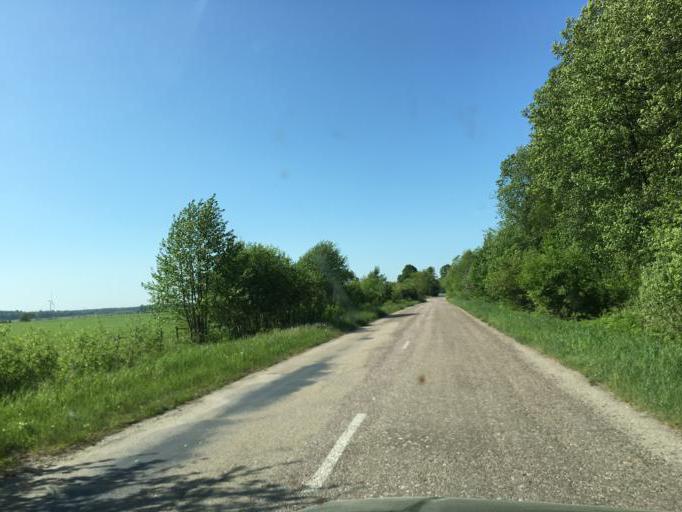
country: LV
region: Ventspils
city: Ventspils
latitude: 57.5027
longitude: 21.8457
